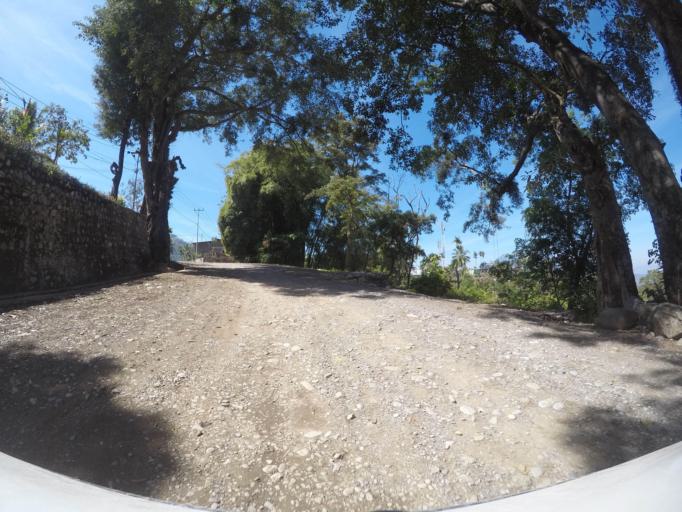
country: TL
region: Ermera
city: Gleno
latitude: -8.8104
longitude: 125.3181
